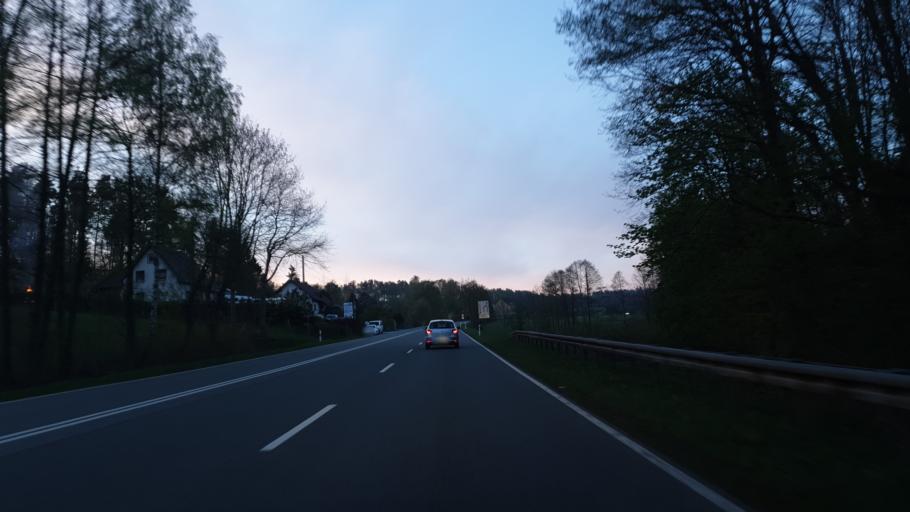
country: DE
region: Saxony
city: Lossnitz
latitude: 50.6366
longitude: 12.7336
